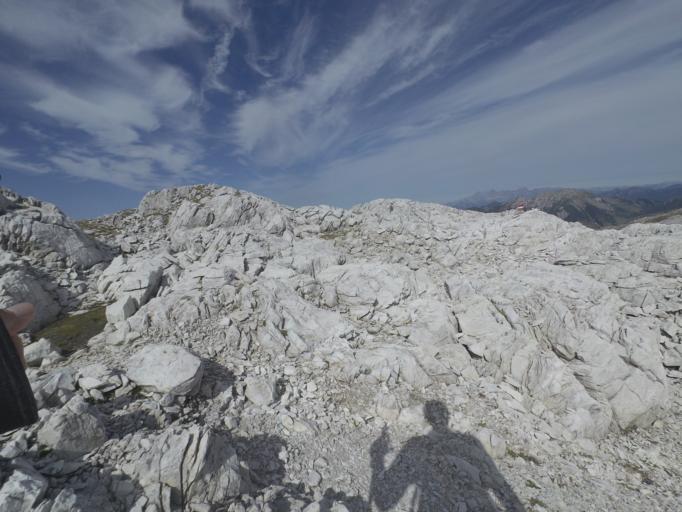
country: AT
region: Salzburg
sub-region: Politischer Bezirk Sankt Johann im Pongau
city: Kleinarl
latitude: 47.2166
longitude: 13.3905
